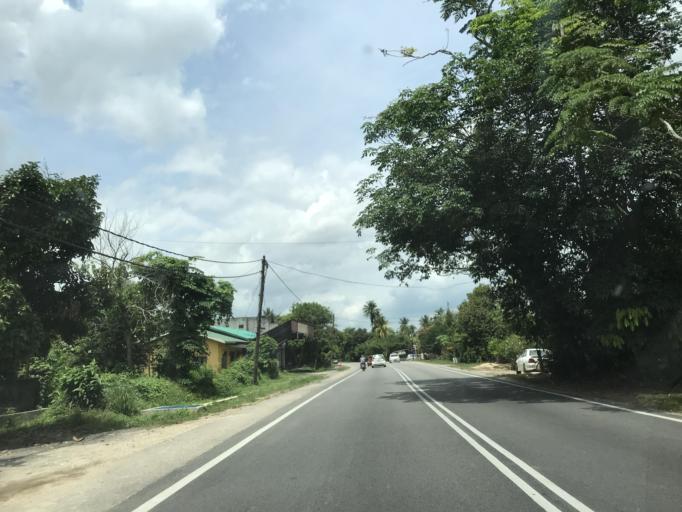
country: MY
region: Kelantan
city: Kota Bharu
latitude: 6.0934
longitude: 102.2084
